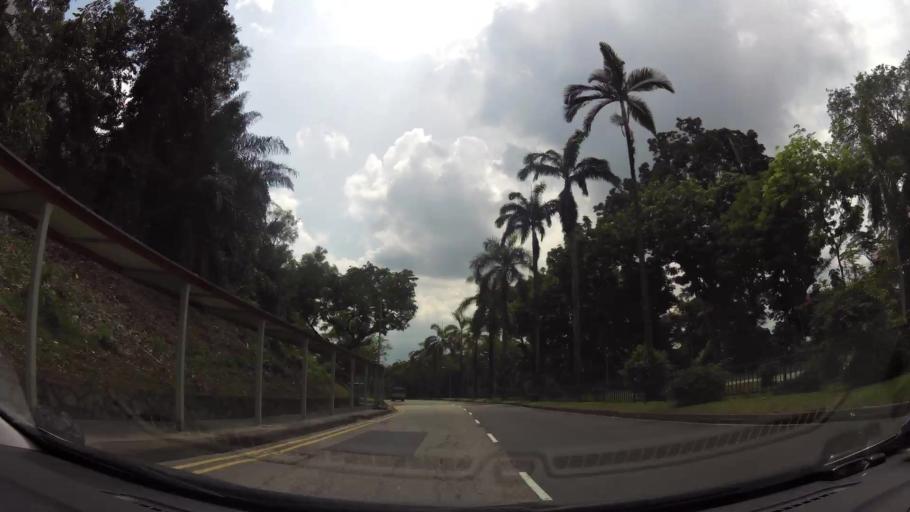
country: MY
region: Johor
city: Johor Bahru
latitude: 1.4291
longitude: 103.7621
